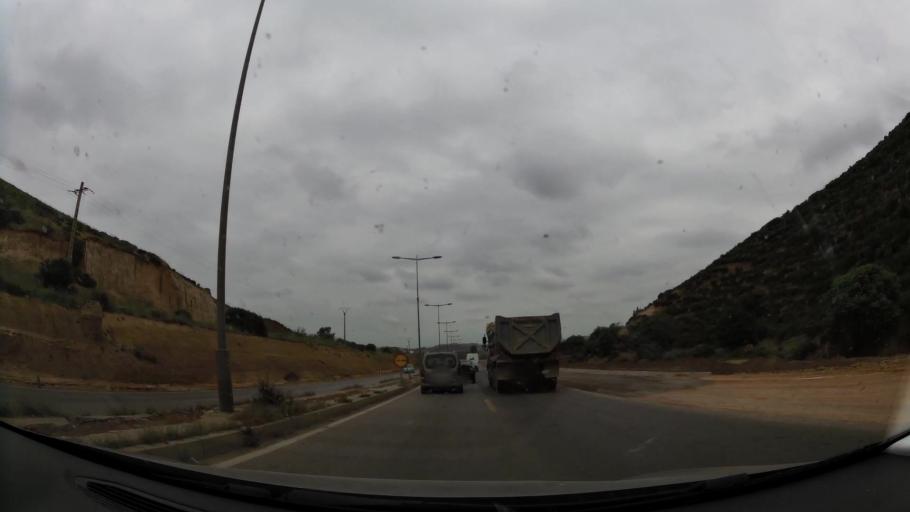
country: MA
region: Rabat-Sale-Zemmour-Zaer
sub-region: Rabat
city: Rabat
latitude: 33.9805
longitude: -6.8039
